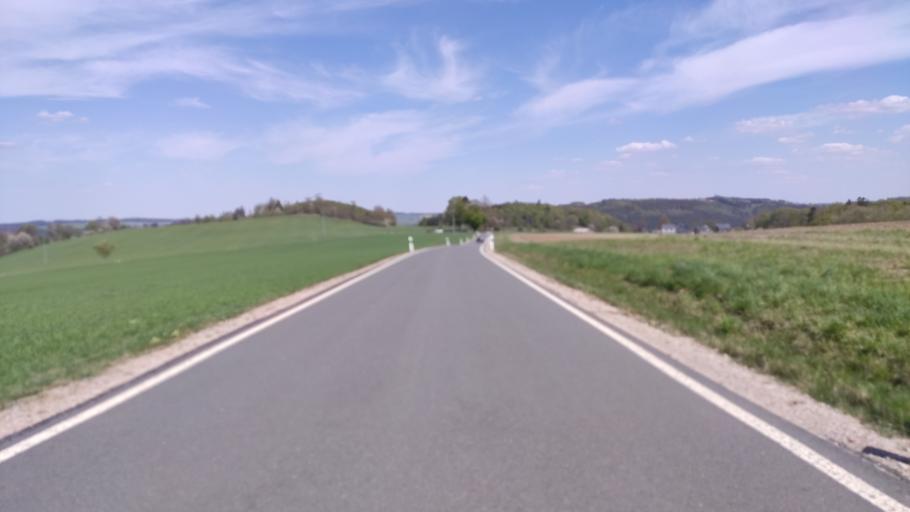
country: DE
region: Thuringia
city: Leutenberg
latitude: 50.4923
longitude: 11.4656
